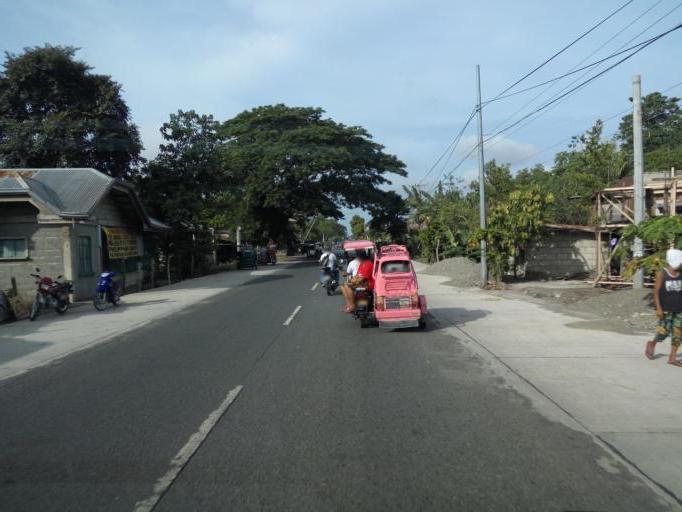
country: PH
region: Cagayan Valley
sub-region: Province of Isabela
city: Cabagan
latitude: 17.4351
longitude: 121.7764
